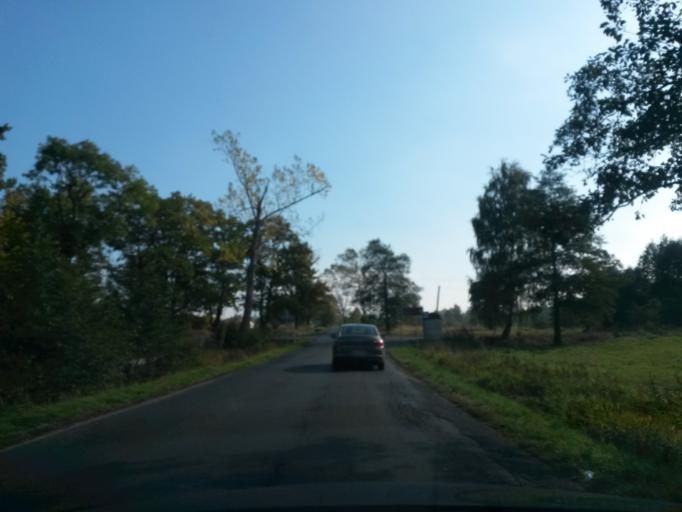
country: PL
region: Lower Silesian Voivodeship
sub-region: Powiat jeleniogorski
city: Sosnowka
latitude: 50.8153
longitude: 15.7546
